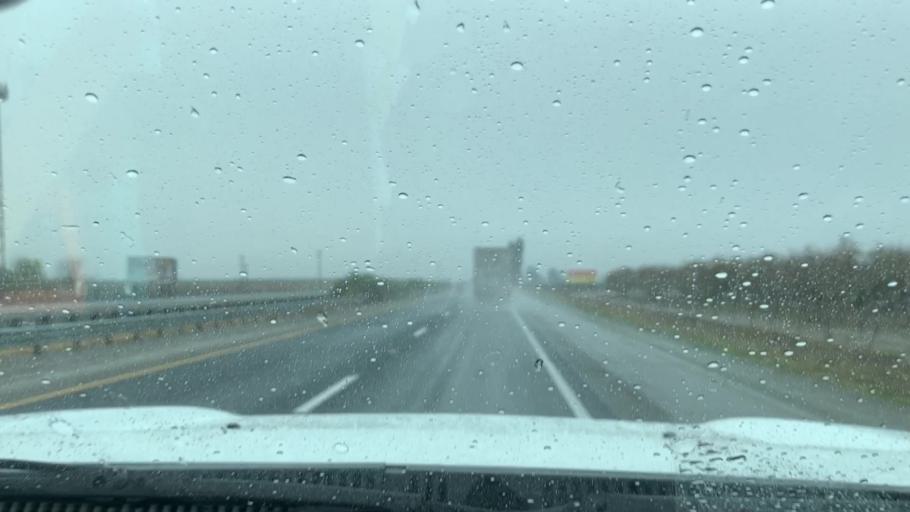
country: US
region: California
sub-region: Tulare County
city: Earlimart
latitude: 35.8610
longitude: -119.2686
